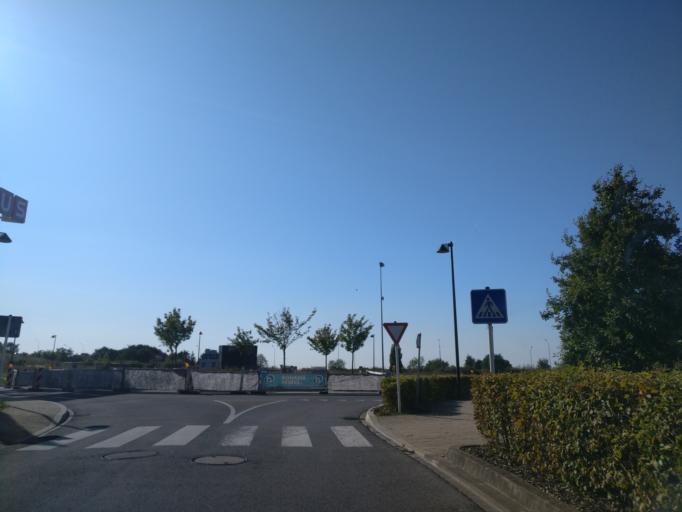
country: LU
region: Luxembourg
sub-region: Canton de Capellen
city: Mamer
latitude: 49.6407
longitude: 6.0139
